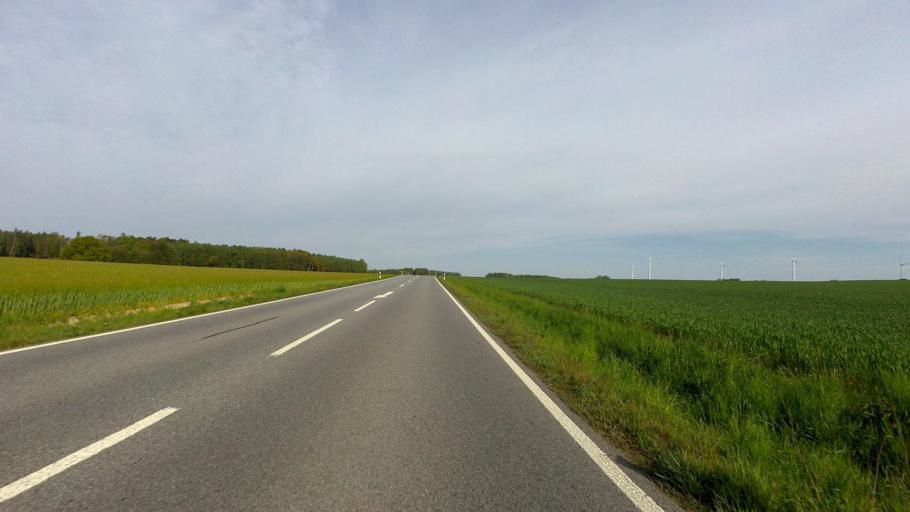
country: DE
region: Saxony
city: Stolpen
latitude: 51.0634
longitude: 14.0565
